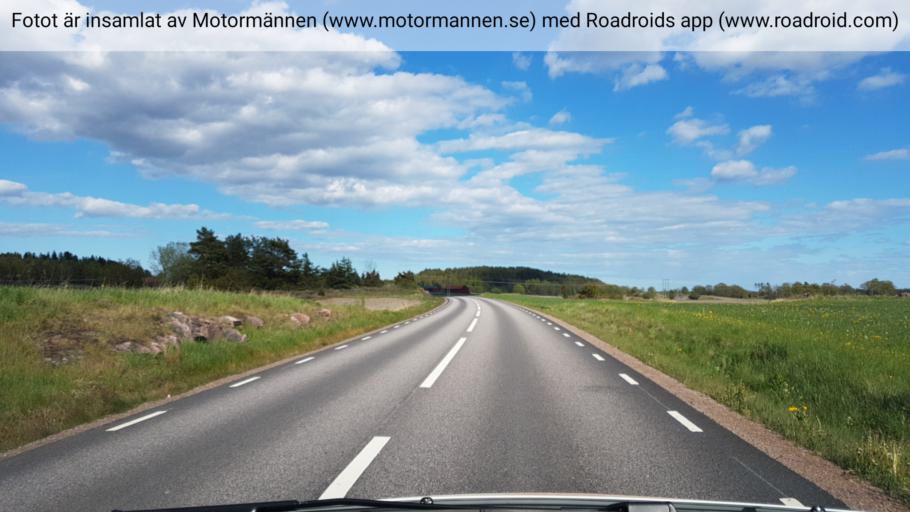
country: SE
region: Kalmar
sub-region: Vasterviks Kommun
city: Forserum
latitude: 57.9383
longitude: 16.4657
